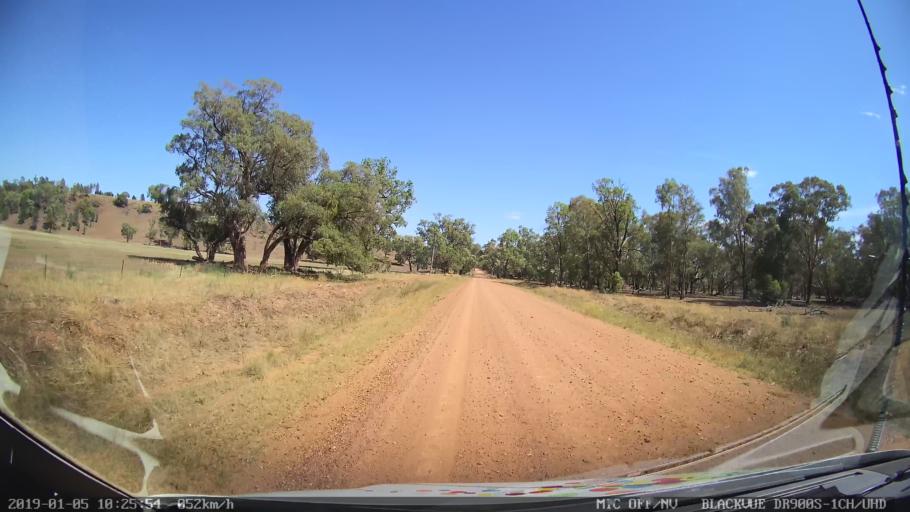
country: AU
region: New South Wales
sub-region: Gilgandra
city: Gilgandra
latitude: -31.5577
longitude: 148.9572
